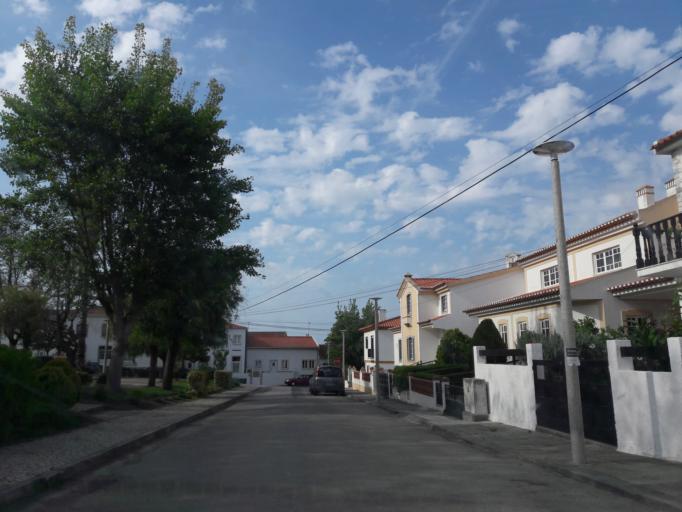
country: PT
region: Leiria
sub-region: Peniche
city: Atouguia da Baleia
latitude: 39.3361
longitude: -9.3247
